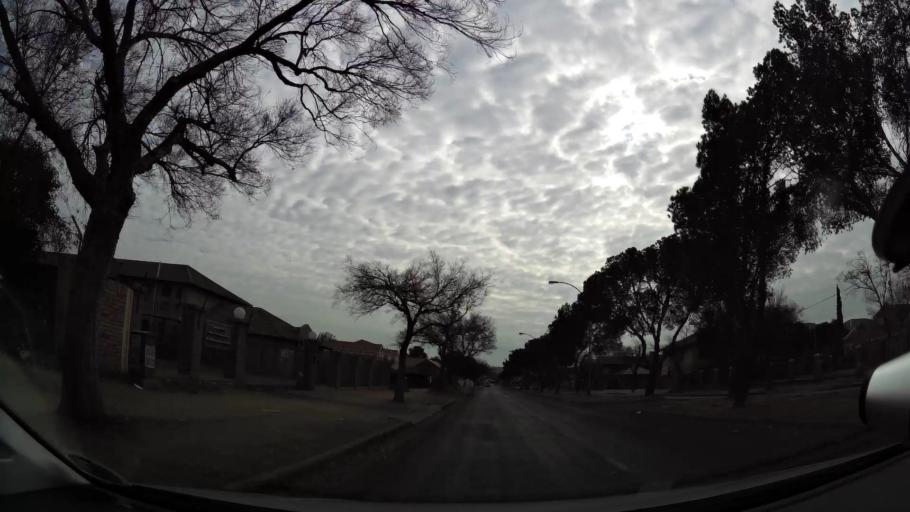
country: ZA
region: Orange Free State
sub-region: Mangaung Metropolitan Municipality
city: Bloemfontein
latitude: -29.1239
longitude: 26.2030
